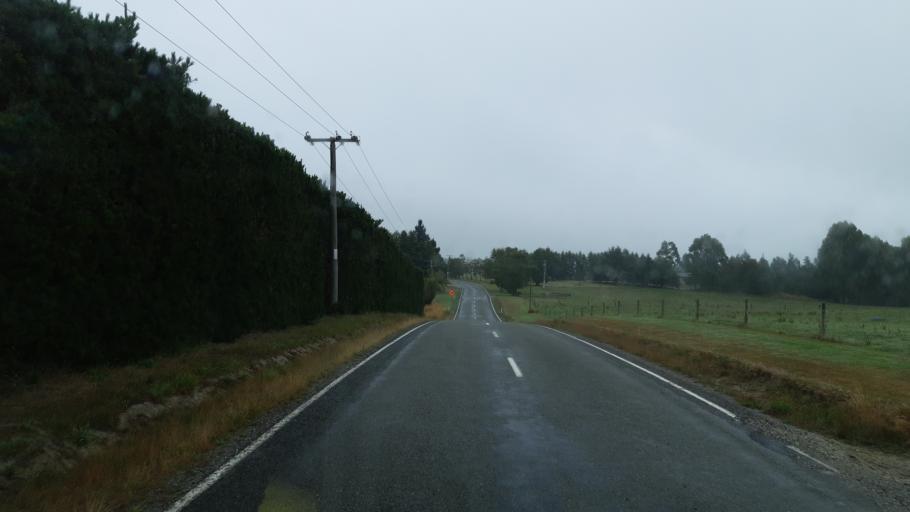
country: NZ
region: Otago
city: Oamaru
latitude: -44.9291
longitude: 170.7929
